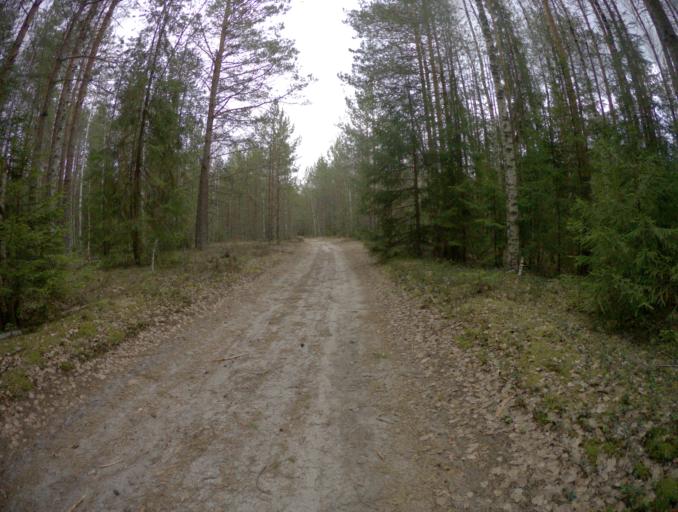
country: RU
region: Vladimir
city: Raduzhnyy
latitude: 55.9495
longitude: 40.2646
